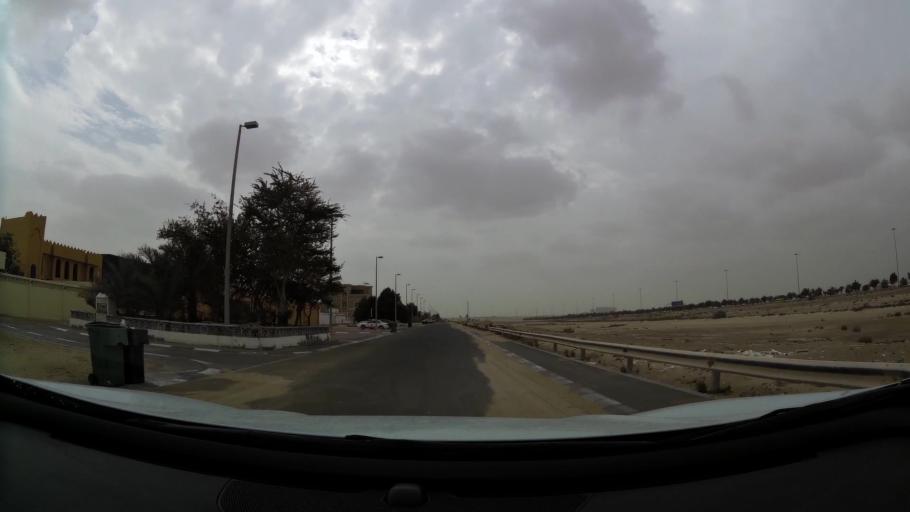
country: AE
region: Abu Dhabi
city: Abu Dhabi
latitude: 24.3482
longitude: 54.6446
